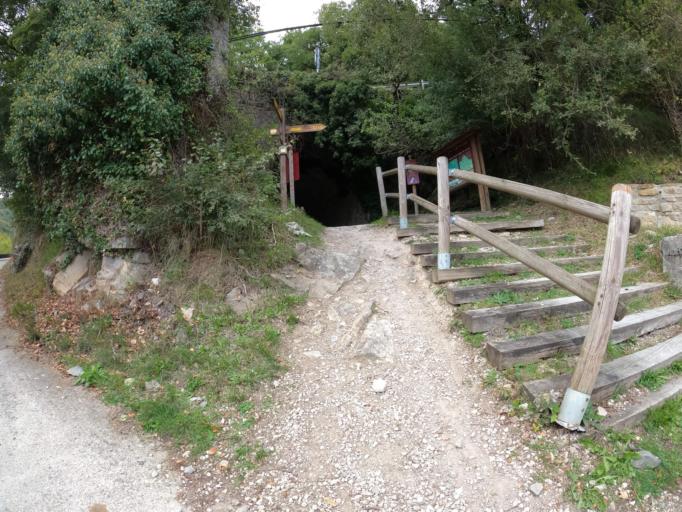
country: ES
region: Navarre
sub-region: Provincia de Navarra
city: Irurtzun
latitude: 42.9626
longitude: -1.8280
